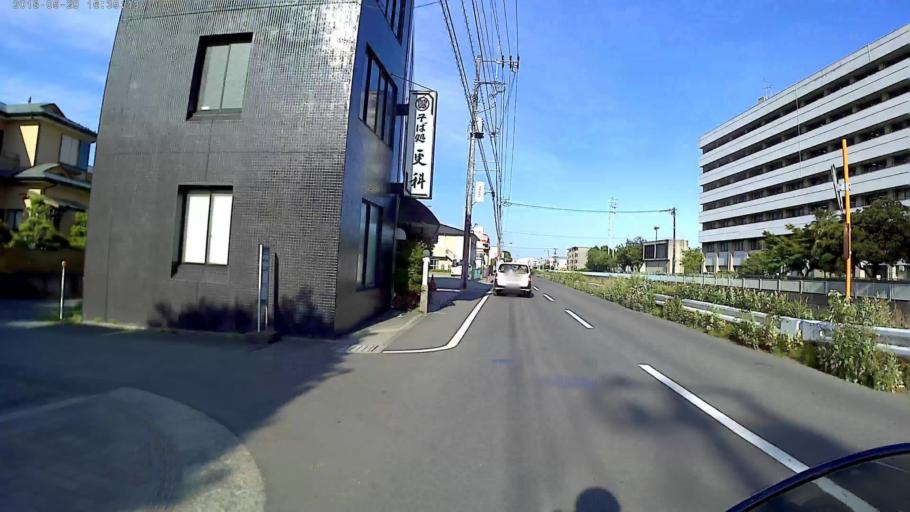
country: JP
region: Kanagawa
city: Odawara
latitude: 35.2686
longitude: 139.1515
